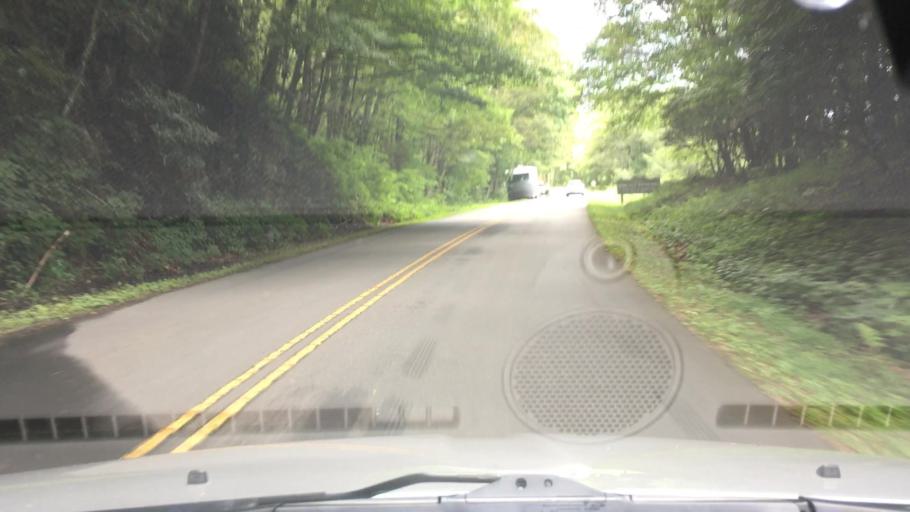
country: US
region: North Carolina
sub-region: Buncombe County
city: Swannanoa
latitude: 35.6782
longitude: -82.4256
